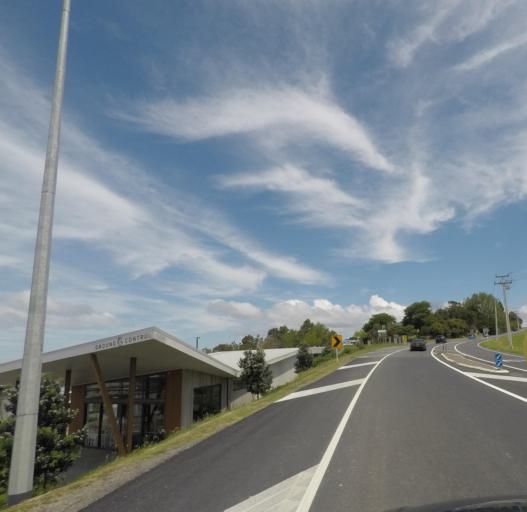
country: NZ
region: Auckland
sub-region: Auckland
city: Rothesay Bay
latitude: -36.6262
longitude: 174.6727
